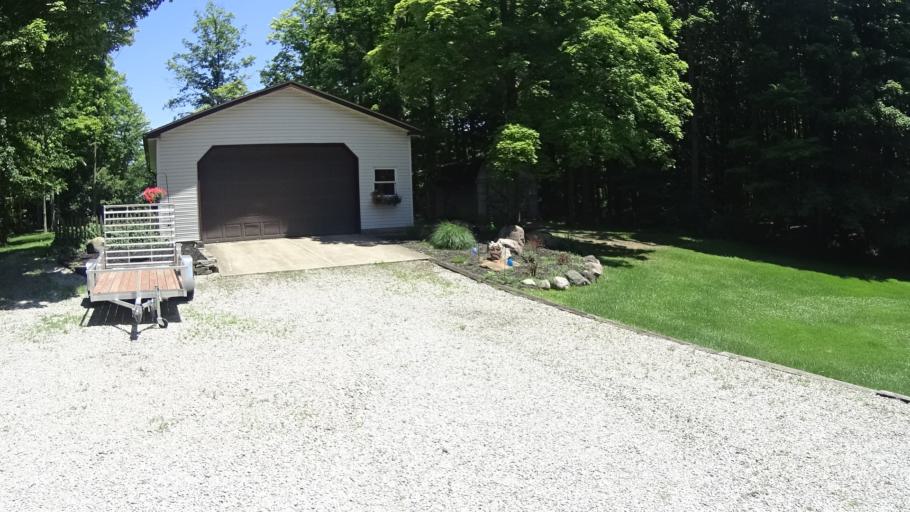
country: US
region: Ohio
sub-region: Lorain County
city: Vermilion
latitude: 41.3541
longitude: -82.3992
